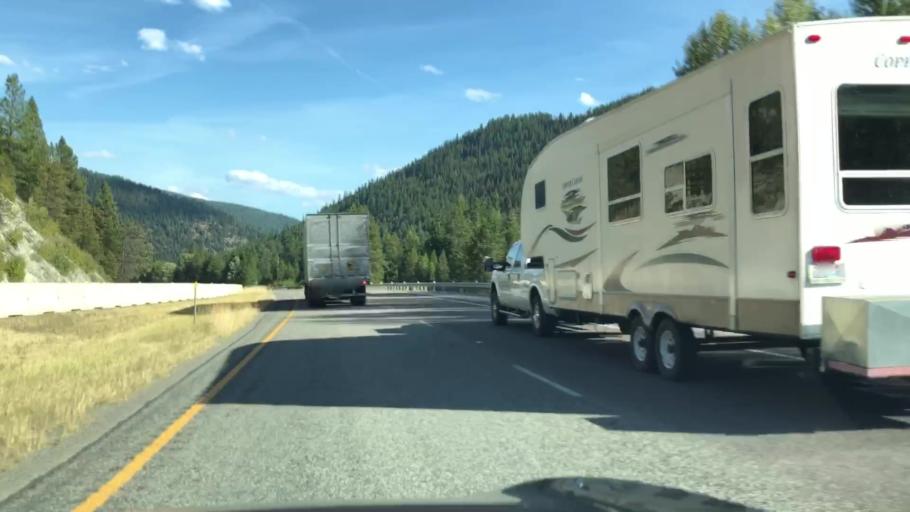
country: US
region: Montana
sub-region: Sanders County
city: Thompson Falls
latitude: 47.3606
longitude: -115.3191
